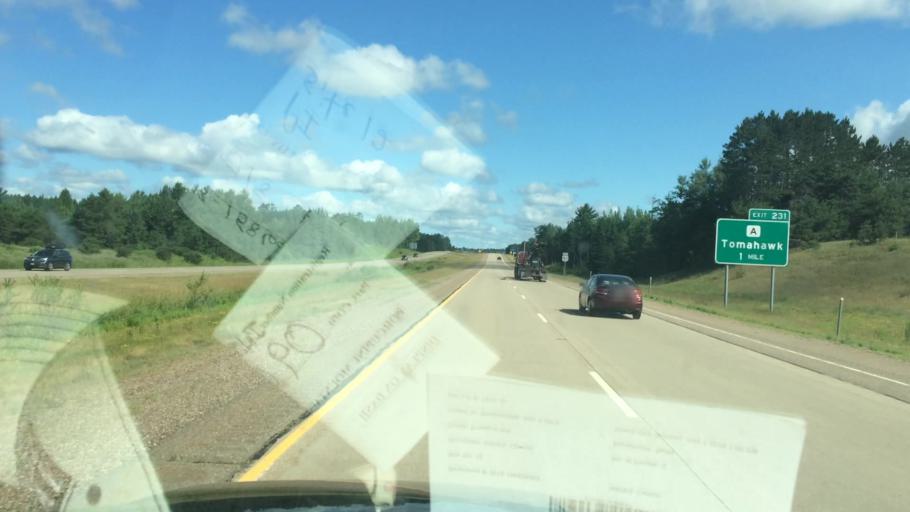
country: US
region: Wisconsin
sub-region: Lincoln County
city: Tomahawk
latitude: 45.4762
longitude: -89.6924
